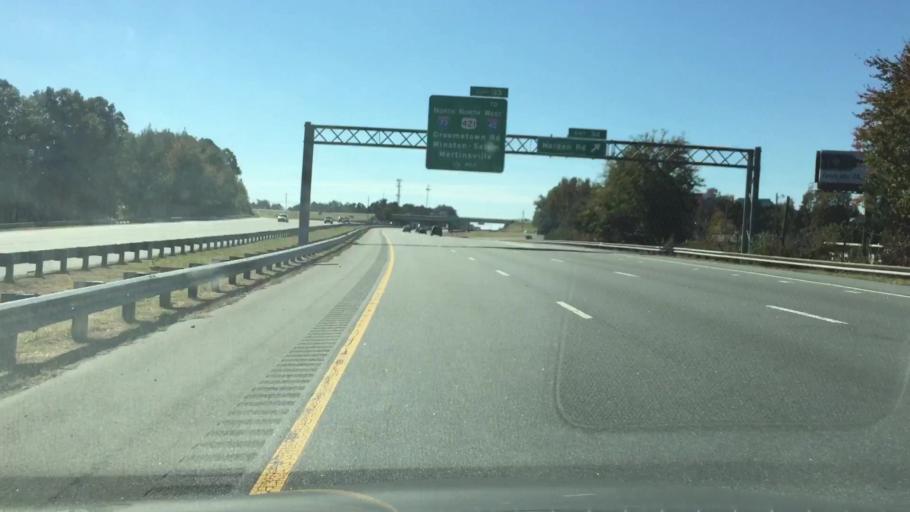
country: US
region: North Carolina
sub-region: Guilford County
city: Greensboro
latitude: 36.0144
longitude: -79.8346
